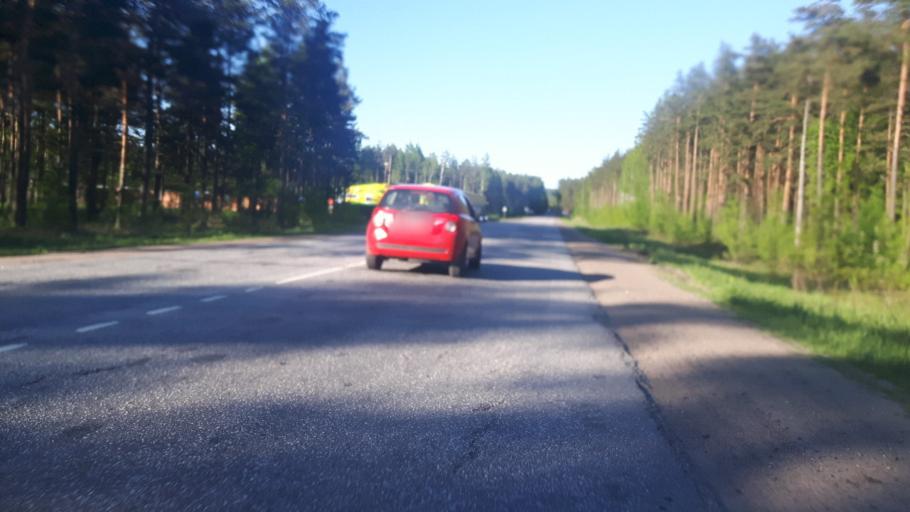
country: RU
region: Leningrad
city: Molodezhnoye
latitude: 60.1725
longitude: 29.4343
